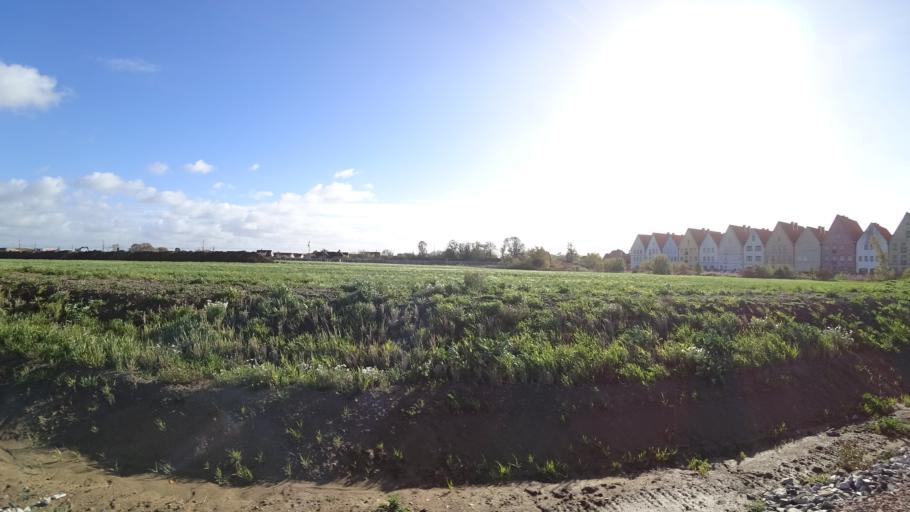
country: SE
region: Skane
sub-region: Staffanstorps Kommun
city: Hjaerup
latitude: 55.6767
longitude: 13.1369
